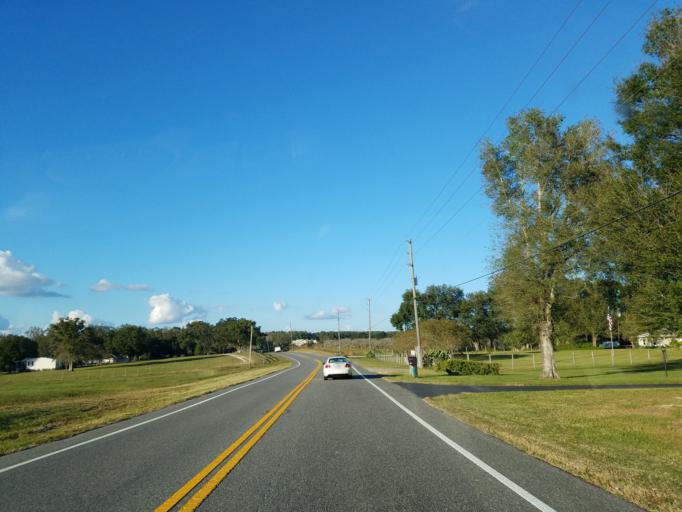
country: US
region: Florida
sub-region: Hernando County
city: Hill 'n Dale
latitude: 28.4632
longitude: -82.3010
